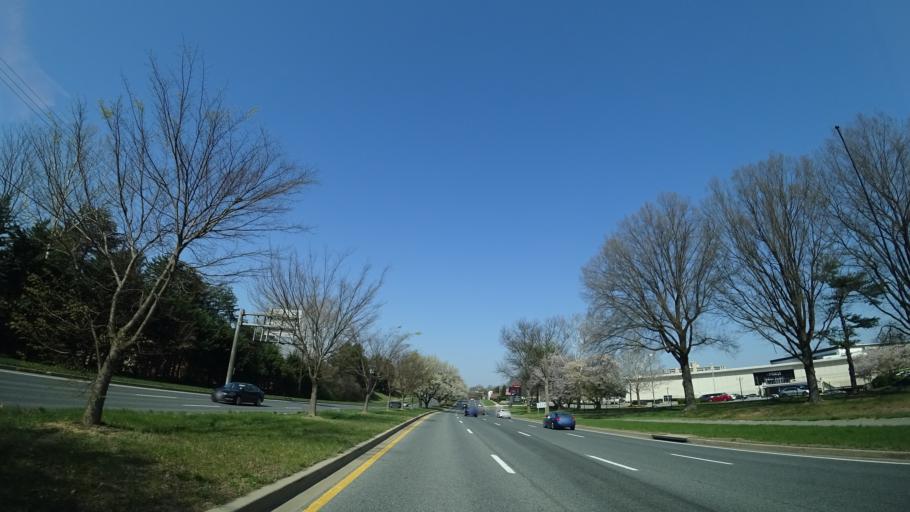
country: US
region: Maryland
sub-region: Montgomery County
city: North Bethesda
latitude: 39.0218
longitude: -77.1454
